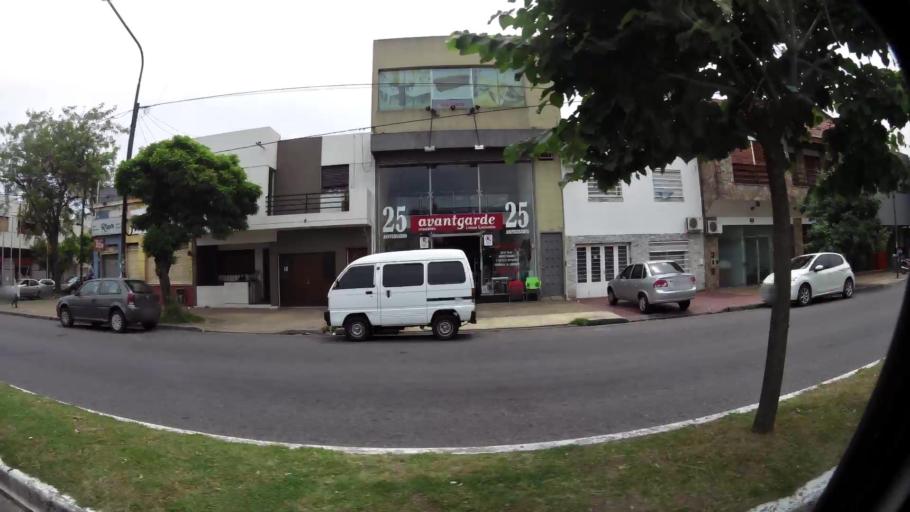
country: AR
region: Buenos Aires
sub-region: Partido de La Plata
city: La Plata
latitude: -34.9244
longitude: -57.9703
